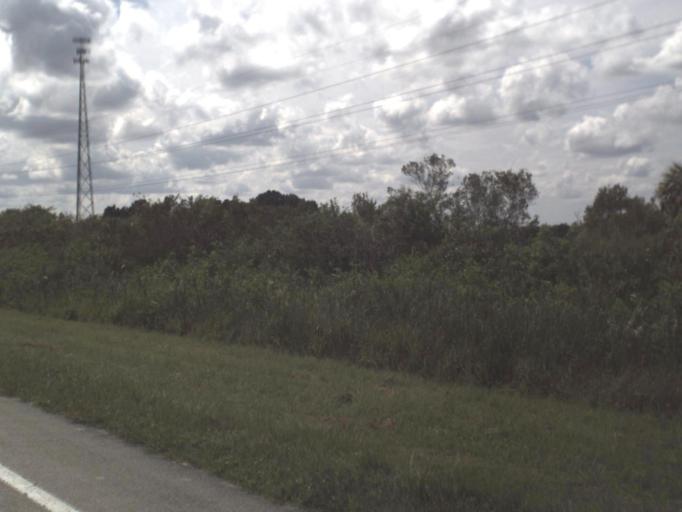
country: US
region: Florida
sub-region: Collier County
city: Orangetree
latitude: 26.1327
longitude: -81.3449
